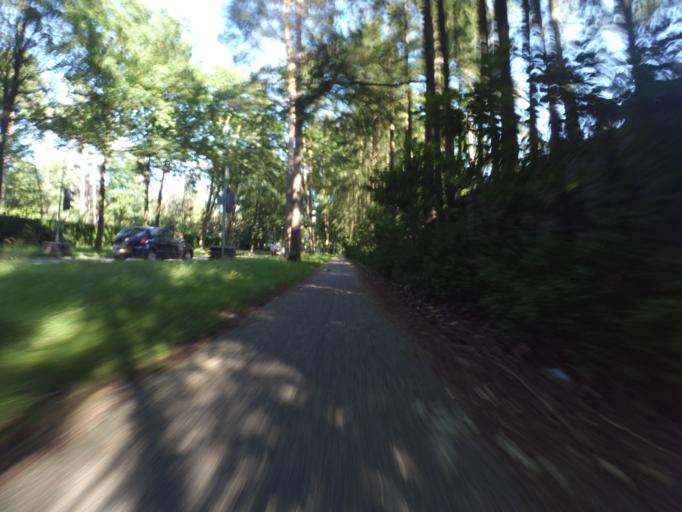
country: NL
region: Utrecht
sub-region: Gemeente Utrechtse Heuvelrug
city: Driebergen-Rijsenburg
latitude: 52.0547
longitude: 5.3027
